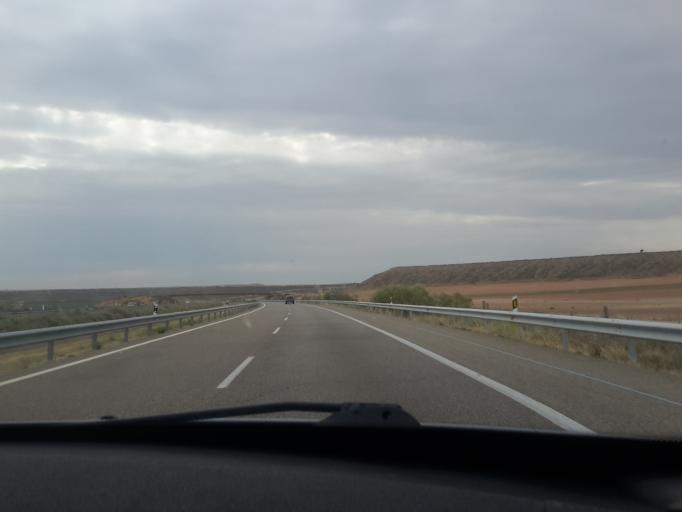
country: ES
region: Aragon
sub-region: Provincia de Huesca
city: Candasnos
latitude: 41.4882
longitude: 0.1679
